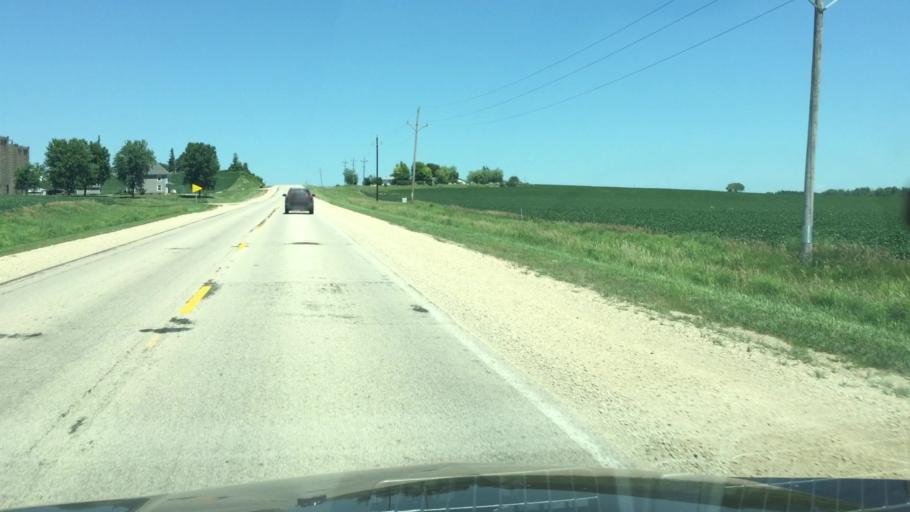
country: US
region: Iowa
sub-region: Cedar County
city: Mechanicsville
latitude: 41.9784
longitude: -91.1417
